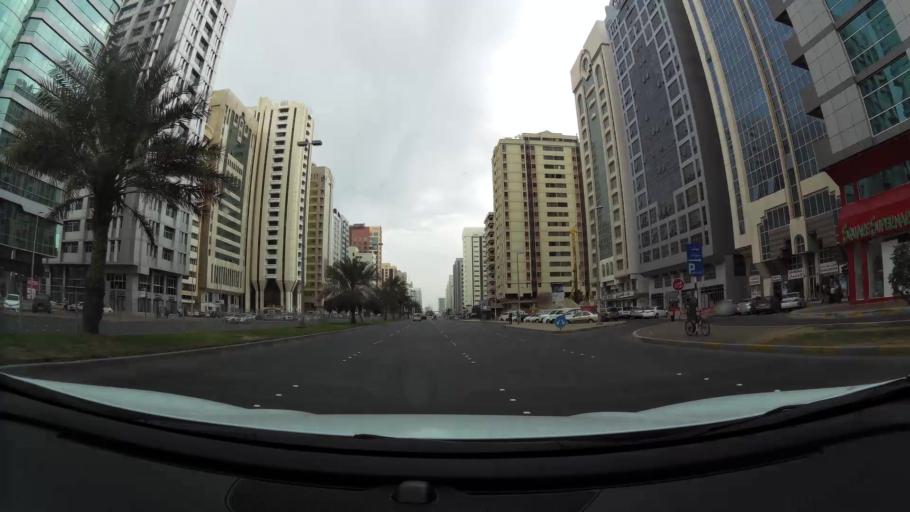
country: AE
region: Abu Dhabi
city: Abu Dhabi
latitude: 24.4768
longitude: 54.3669
